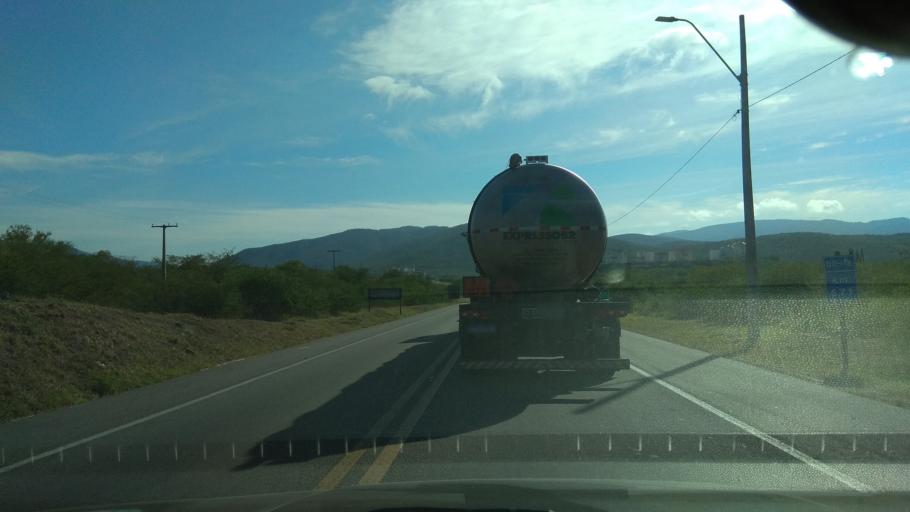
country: BR
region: Bahia
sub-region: Jequie
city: Jequie
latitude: -13.8434
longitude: -40.1106
